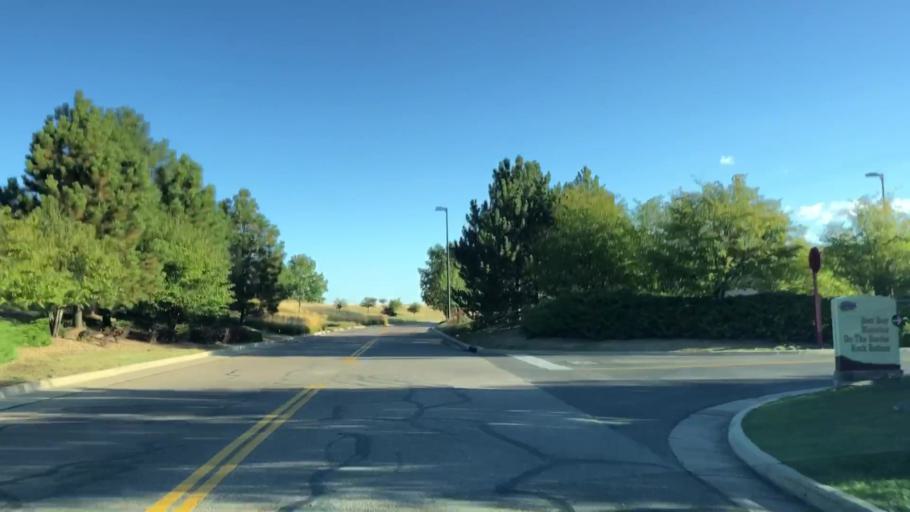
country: US
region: Colorado
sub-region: Larimer County
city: Loveland
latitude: 40.4192
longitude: -104.9919
